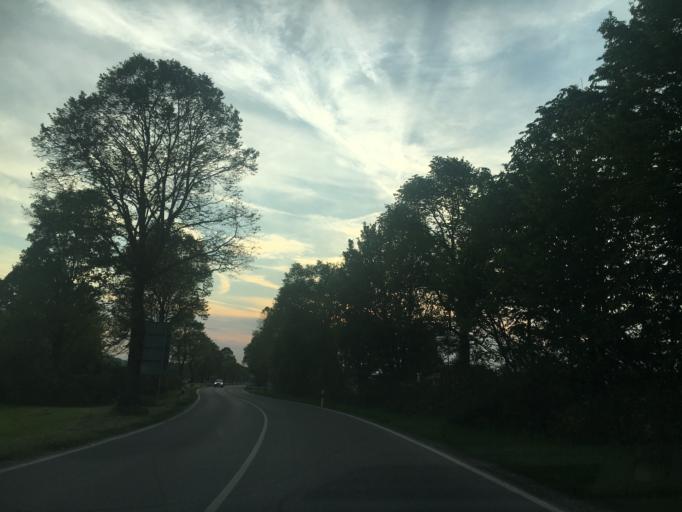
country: DE
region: Bavaria
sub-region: Upper Bavaria
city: Bichl
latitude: 47.7164
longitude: 11.4119
